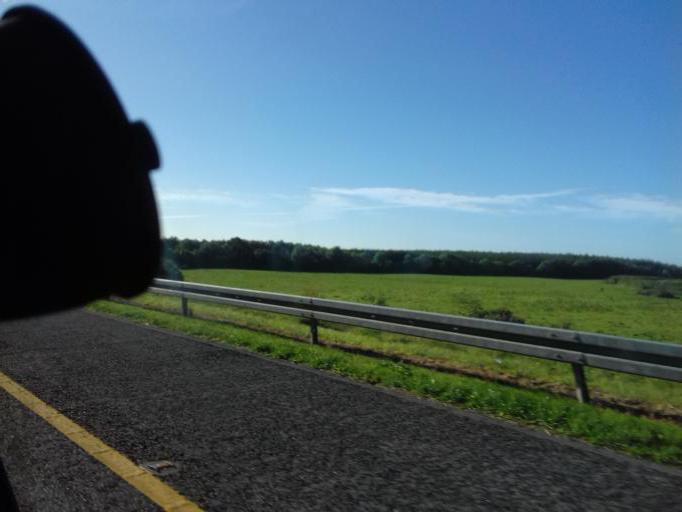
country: IE
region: Leinster
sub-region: An Mhi
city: Longwood
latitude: 53.4276
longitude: -6.9874
